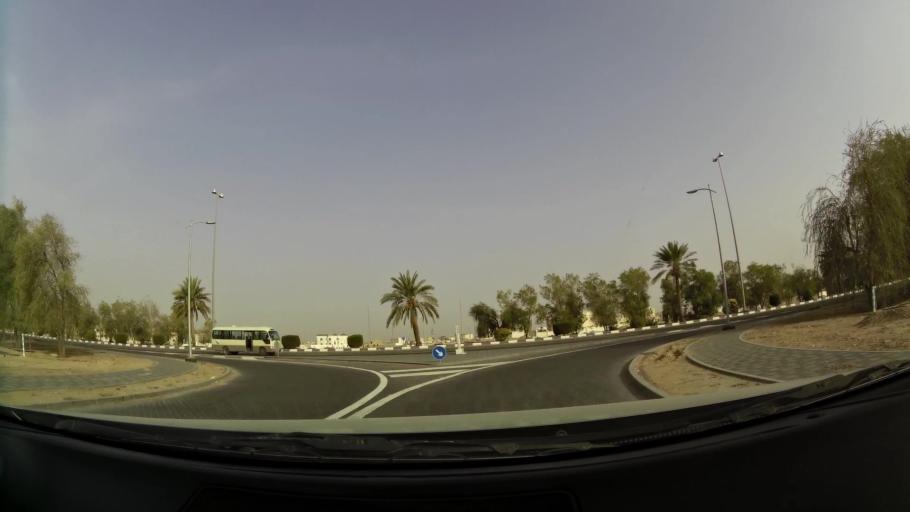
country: AE
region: Abu Dhabi
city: Al Ain
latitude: 24.1060
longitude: 55.6968
